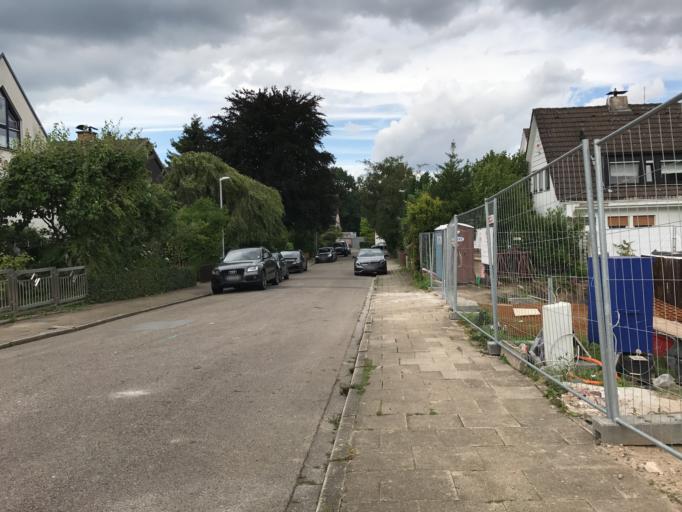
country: DE
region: North Rhine-Westphalia
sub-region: Regierungsbezirk Dusseldorf
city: Muelheim (Ruhr)
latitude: 51.4194
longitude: 6.8293
